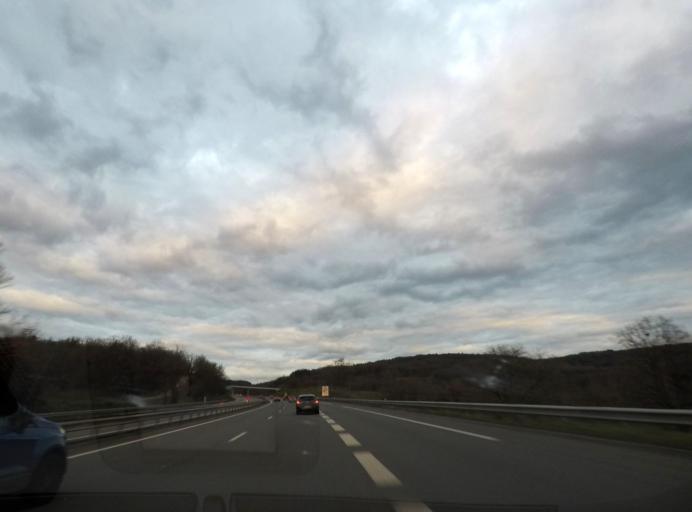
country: FR
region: Rhone-Alpes
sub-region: Departement de l'Ain
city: Poncin
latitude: 46.0953
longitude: 5.4223
